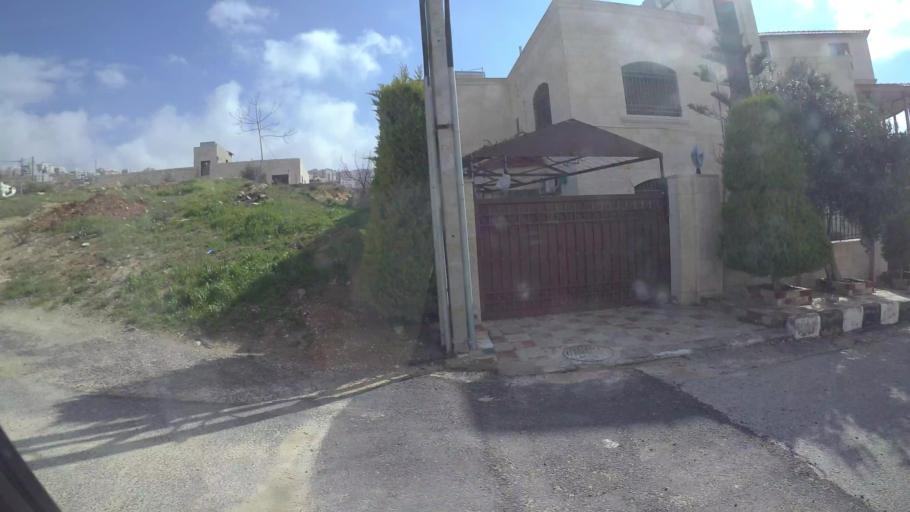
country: JO
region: Amman
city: Al Jubayhah
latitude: 32.0710
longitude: 35.8711
